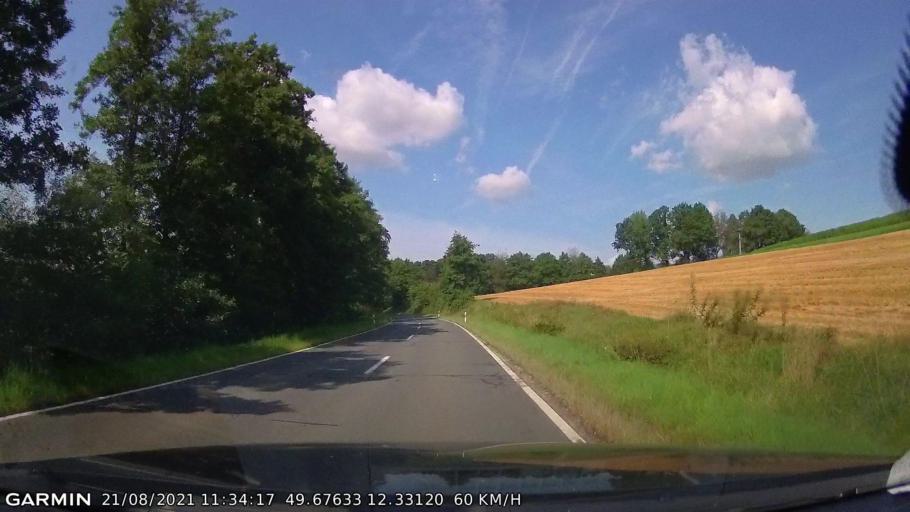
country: DE
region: Bavaria
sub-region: Upper Palatinate
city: Waldthurn
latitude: 49.6763
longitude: 12.3312
